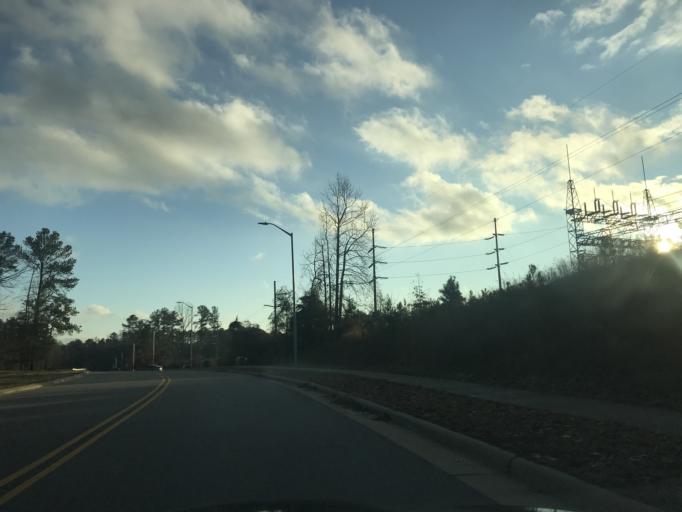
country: US
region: North Carolina
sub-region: Wake County
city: Wake Forest
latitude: 35.9604
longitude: -78.5339
